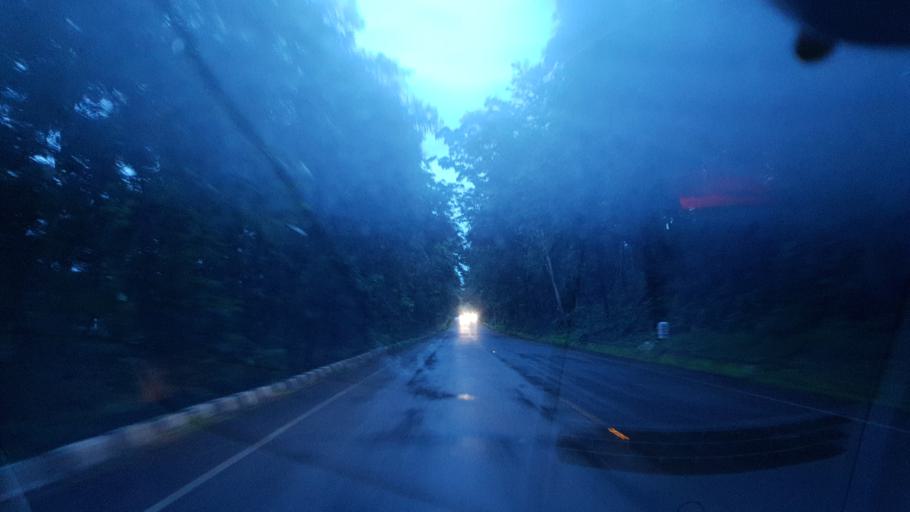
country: TH
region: Mae Hong Son
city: Mae La Noi
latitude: 18.4587
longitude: 97.9349
